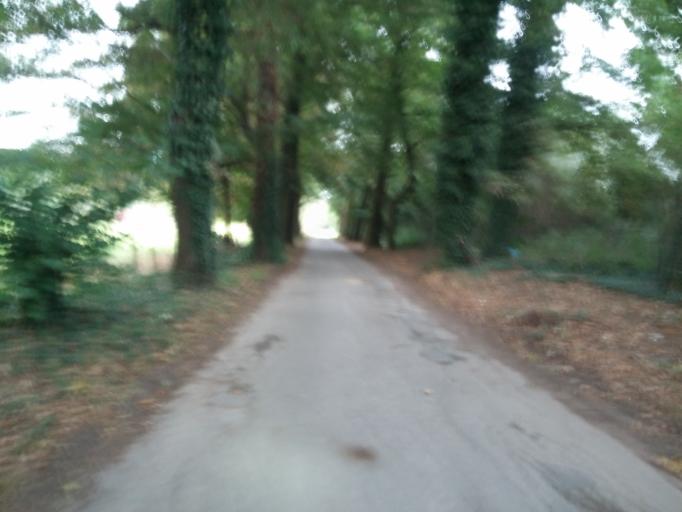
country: DE
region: North Rhine-Westphalia
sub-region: Regierungsbezirk Munster
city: Gladbeck
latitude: 51.6187
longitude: 7.0312
